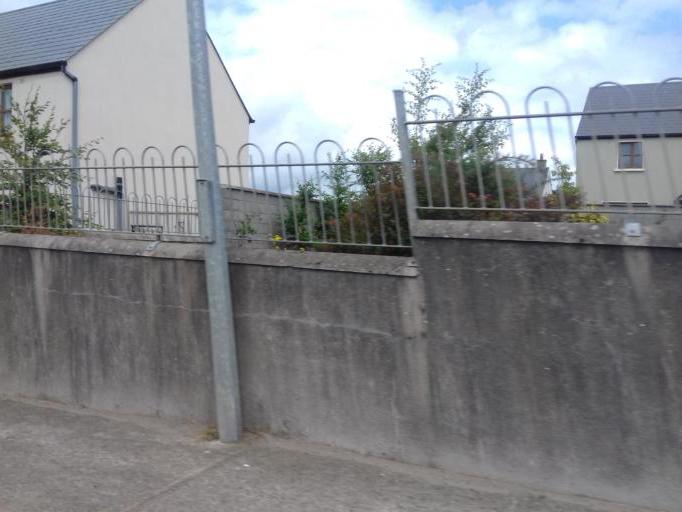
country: IE
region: Leinster
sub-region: Loch Garman
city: Ballinroad
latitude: 52.4775
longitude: -6.4148
